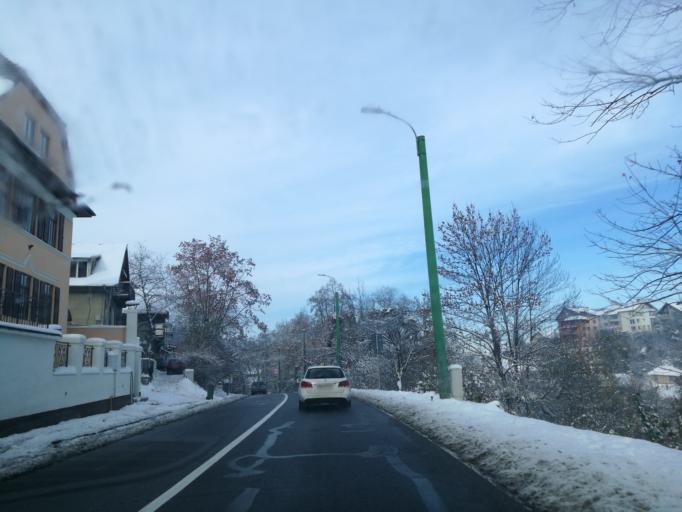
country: RO
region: Brasov
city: Brasov
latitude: 45.6461
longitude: 25.5849
